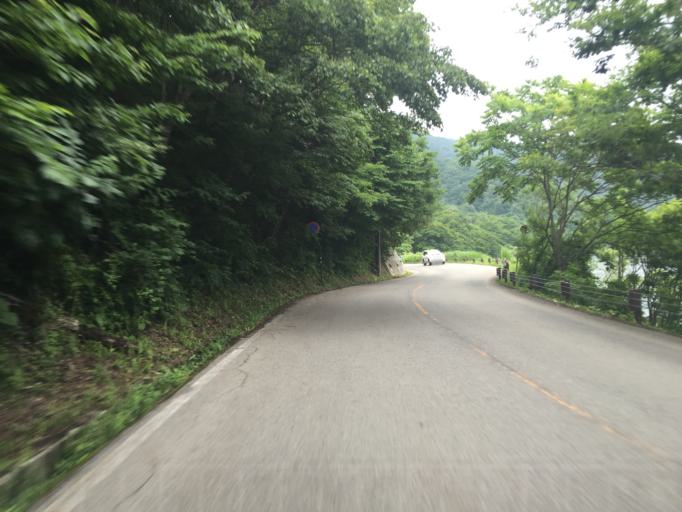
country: JP
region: Fukushima
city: Inawashiro
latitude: 37.7176
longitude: 140.0594
